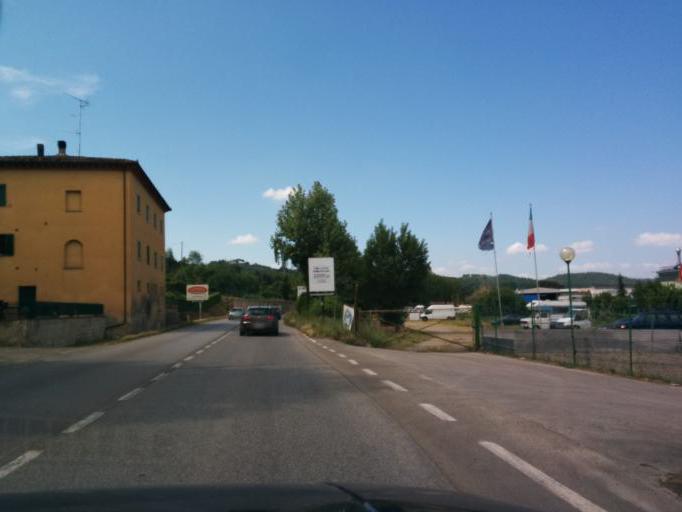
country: IT
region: Tuscany
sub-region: Provincia di Siena
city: Poggibonsi
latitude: 43.4646
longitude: 11.1247
